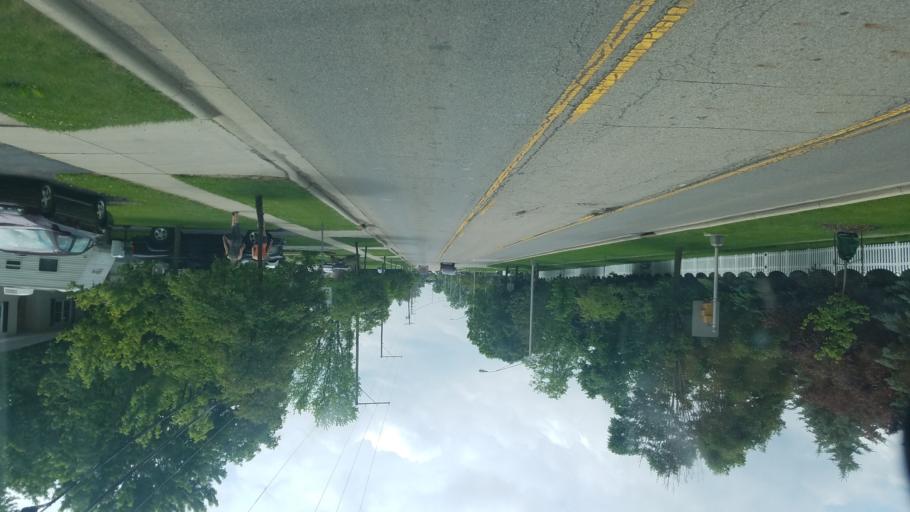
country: US
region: Ohio
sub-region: Franklin County
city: Hilliard
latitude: 40.0413
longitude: -83.1570
